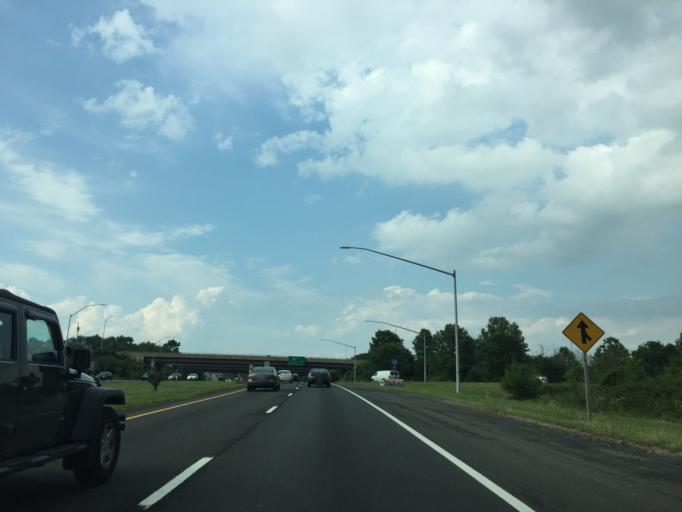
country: US
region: Maryland
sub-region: Howard County
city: Savage
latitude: 39.1368
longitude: -76.8136
